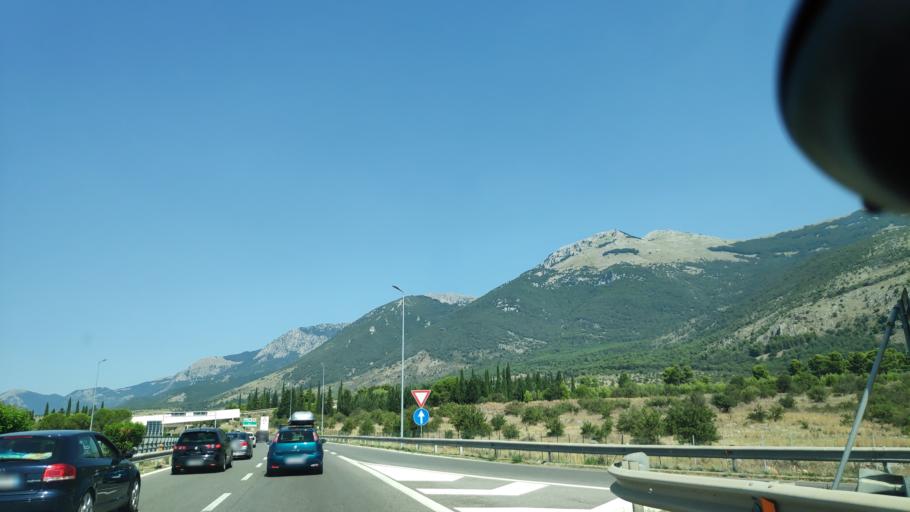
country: IT
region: Calabria
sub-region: Provincia di Cosenza
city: Frascineto
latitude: 39.8367
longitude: 16.2549
